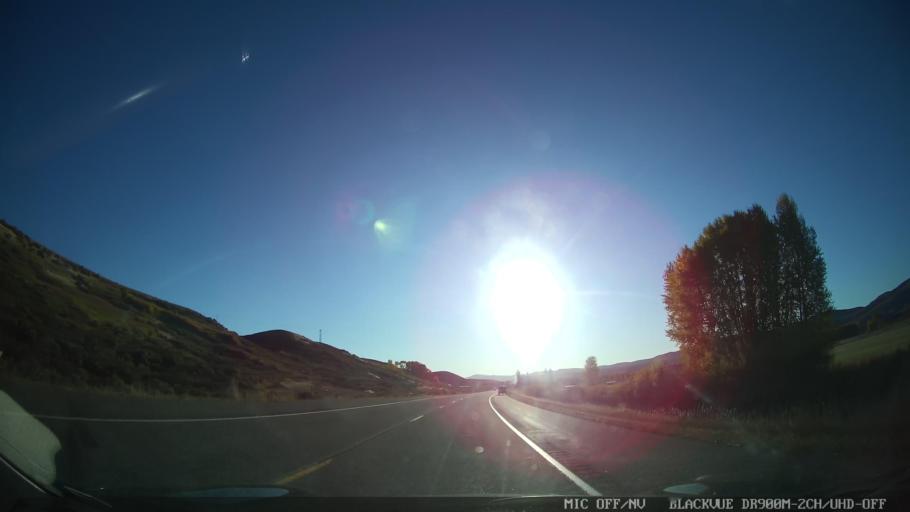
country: US
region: Colorado
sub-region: Grand County
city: Kremmling
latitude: 40.0678
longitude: -106.2673
